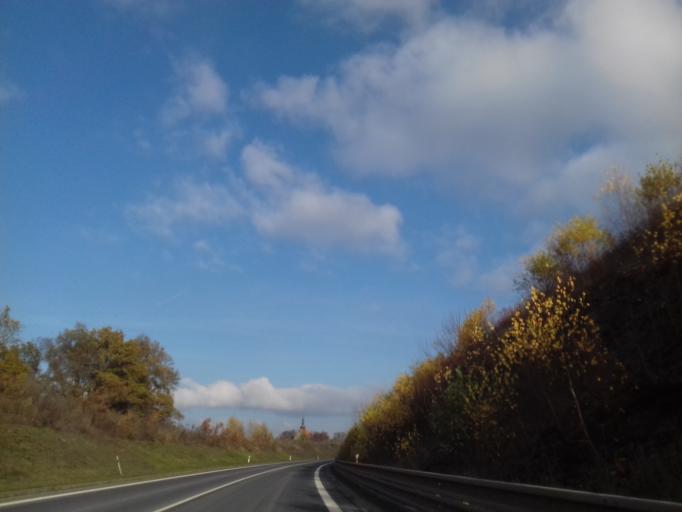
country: CZ
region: Plzensky
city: Horsovsky Tyn
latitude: 49.5171
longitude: 12.9151
